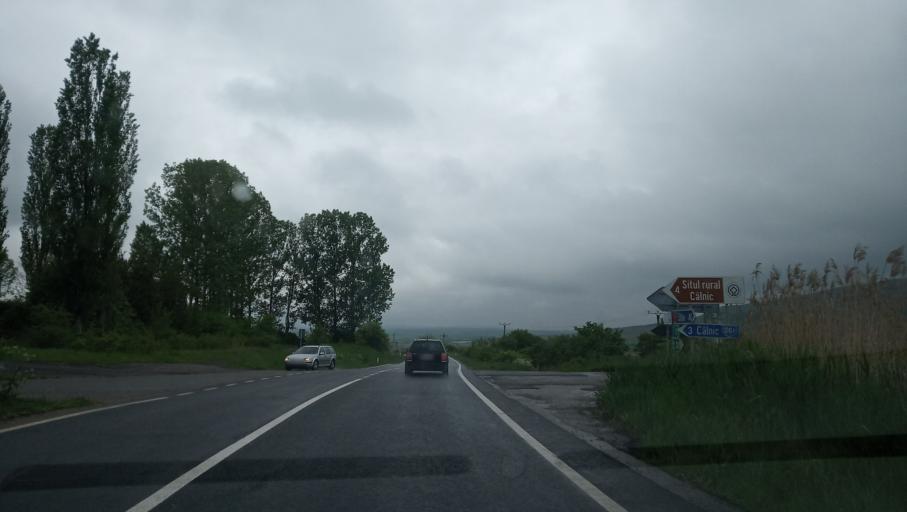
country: RO
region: Alba
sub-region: Comuna Cut
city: Cut
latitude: 45.9201
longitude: 23.6651
